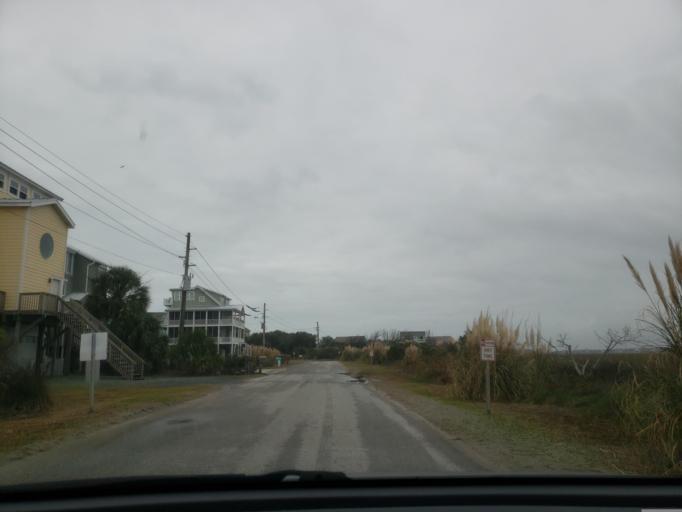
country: US
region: North Carolina
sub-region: Onslow County
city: Sneads Ferry
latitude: 34.5283
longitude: -77.3457
